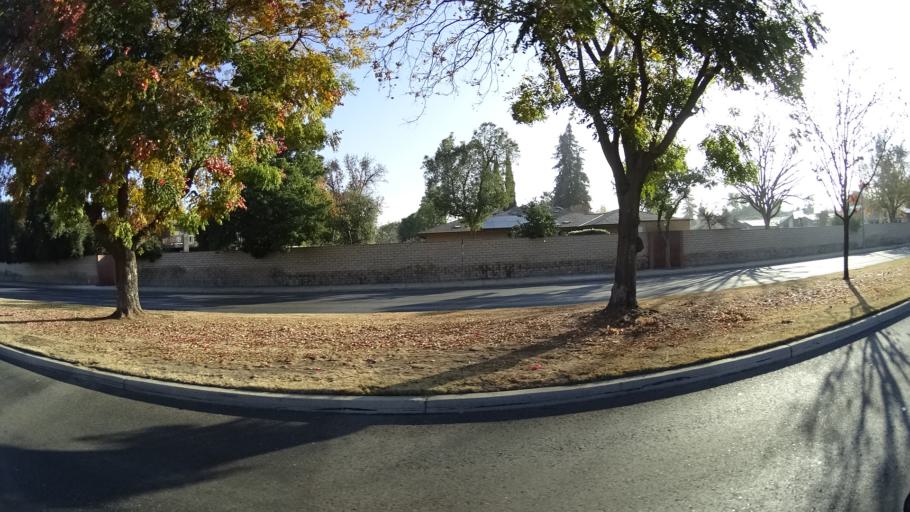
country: US
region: California
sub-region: Kern County
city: Greenacres
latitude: 35.3386
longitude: -119.0923
